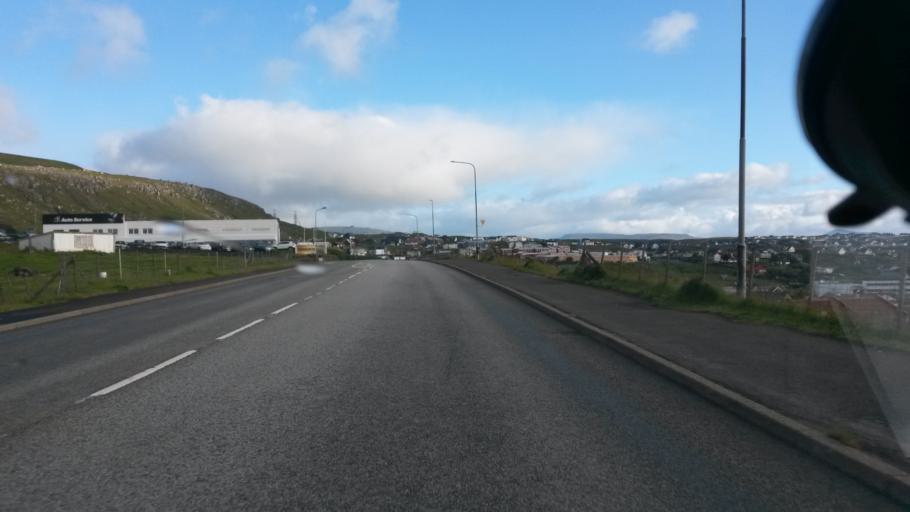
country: FO
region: Streymoy
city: Hoyvik
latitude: 62.0182
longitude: -6.7886
